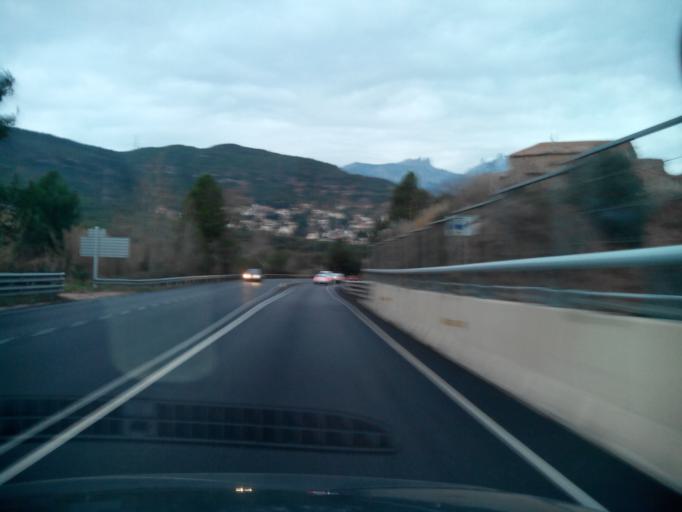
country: ES
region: Catalonia
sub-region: Provincia de Barcelona
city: Olesa de Montserrat
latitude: 41.5911
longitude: 1.9028
